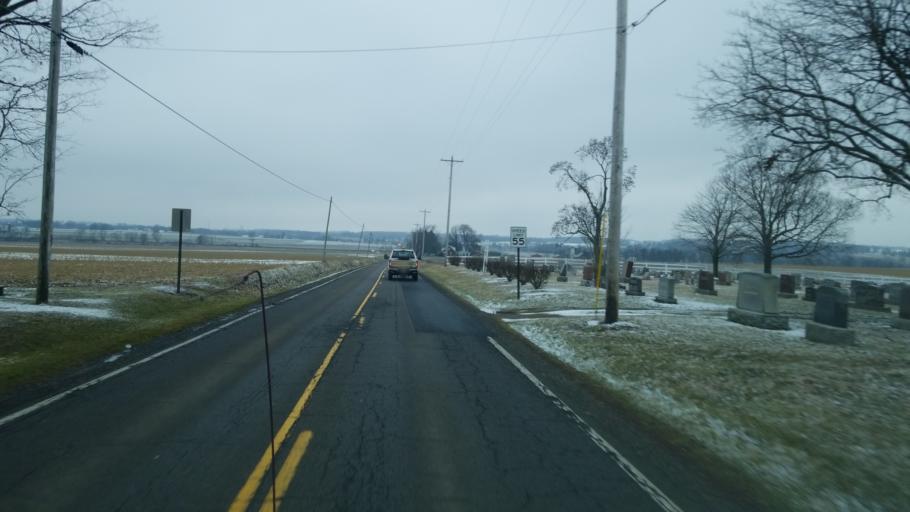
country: US
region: Ohio
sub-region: Wayne County
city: Smithville
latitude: 40.8368
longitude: -81.8424
